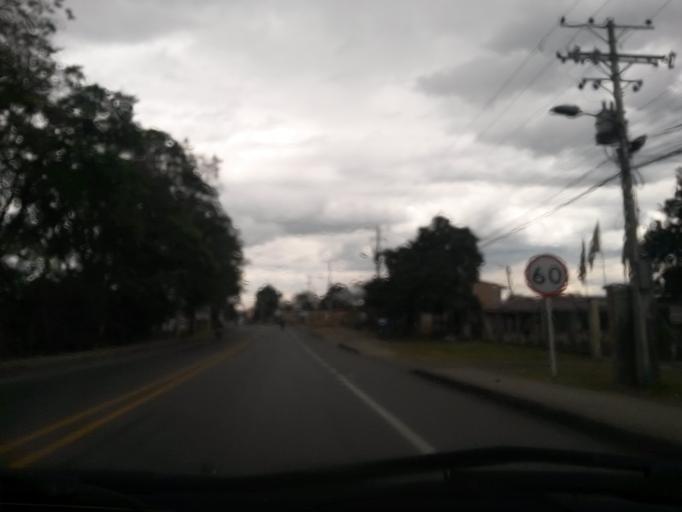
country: CO
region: Cauca
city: Popayan
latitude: 2.5103
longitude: -76.5450
